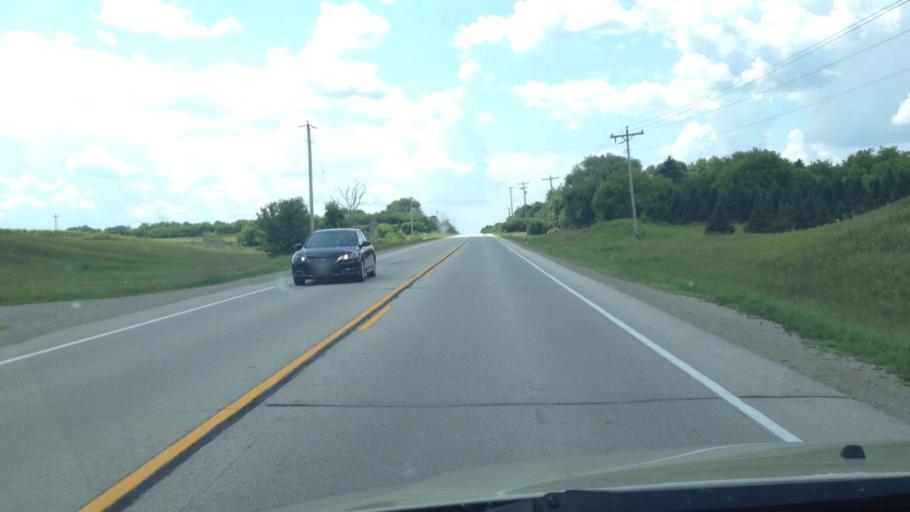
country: US
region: Wisconsin
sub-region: Brown County
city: Suamico
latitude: 44.6480
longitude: -88.1331
